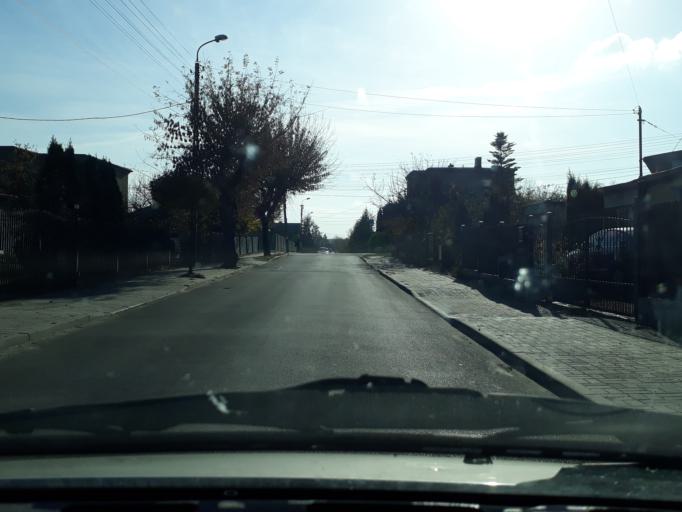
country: PL
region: Silesian Voivodeship
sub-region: Powiat tarnogorski
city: Tarnowskie Gory
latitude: 50.4323
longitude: 18.8441
